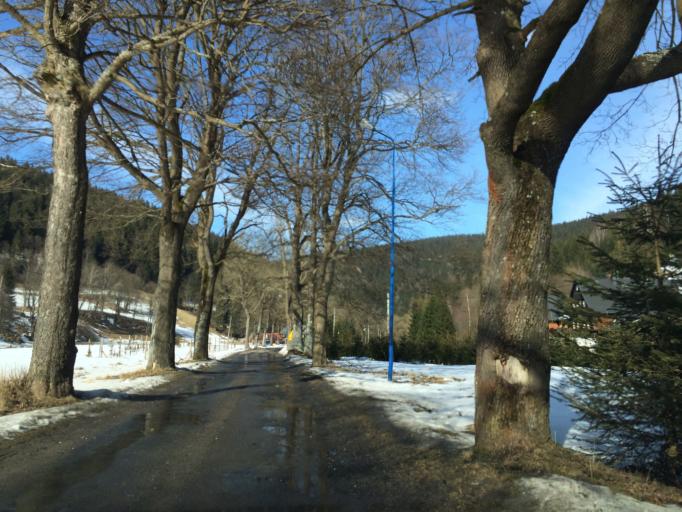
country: CZ
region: Olomoucky
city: Vapenna
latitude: 50.2754
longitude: 17.0065
